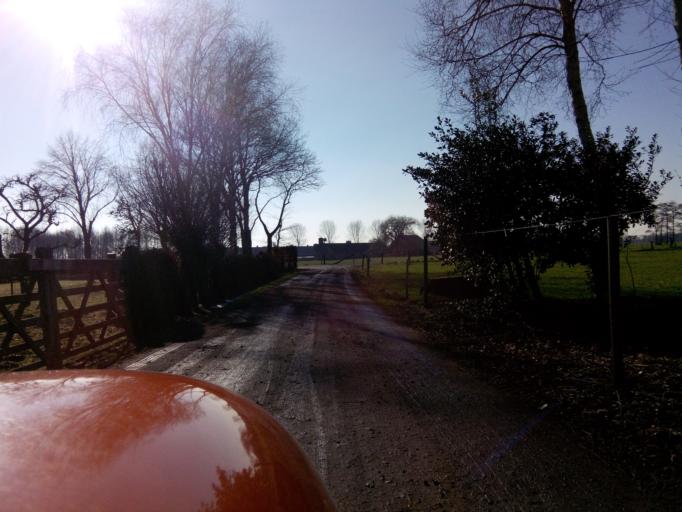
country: NL
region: Gelderland
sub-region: Gemeente Barneveld
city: Barneveld
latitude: 52.1271
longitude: 5.5439
